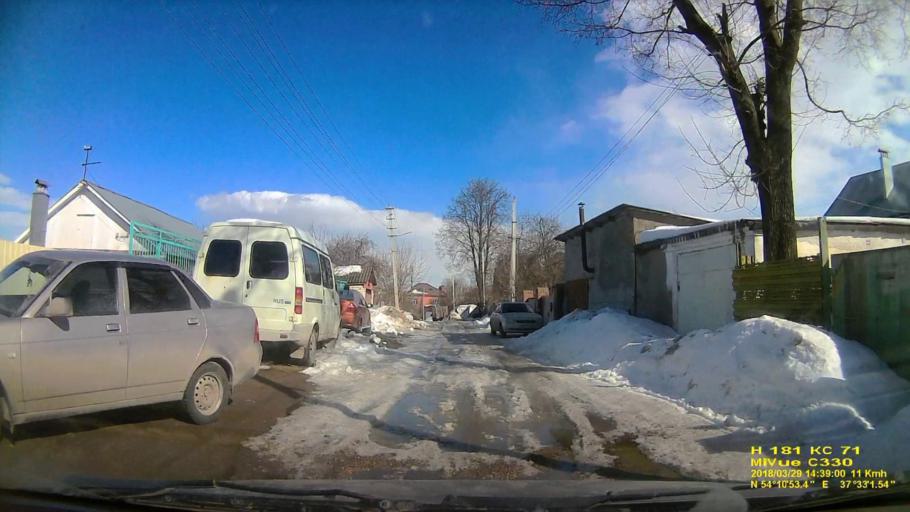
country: RU
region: Tula
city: Mendeleyevskiy
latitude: 54.1815
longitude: 37.5505
